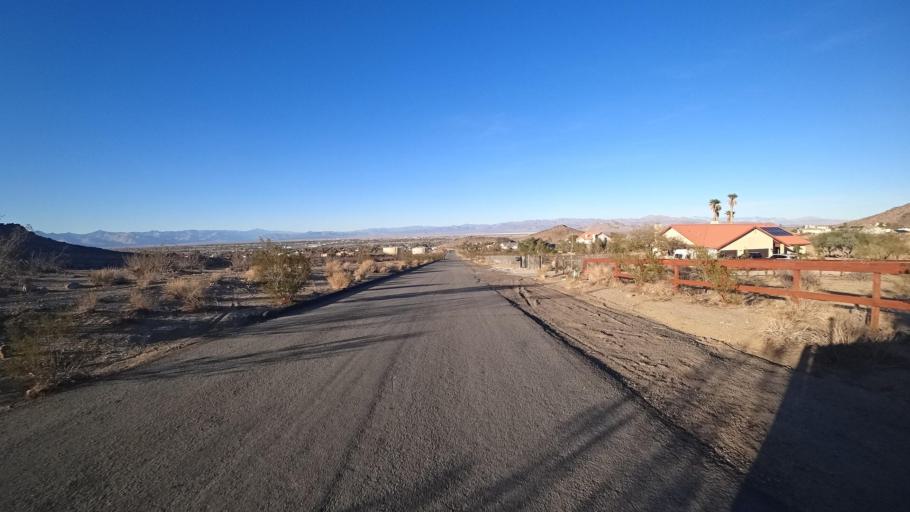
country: US
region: California
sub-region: Kern County
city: Ridgecrest
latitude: 35.5738
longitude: -117.6524
